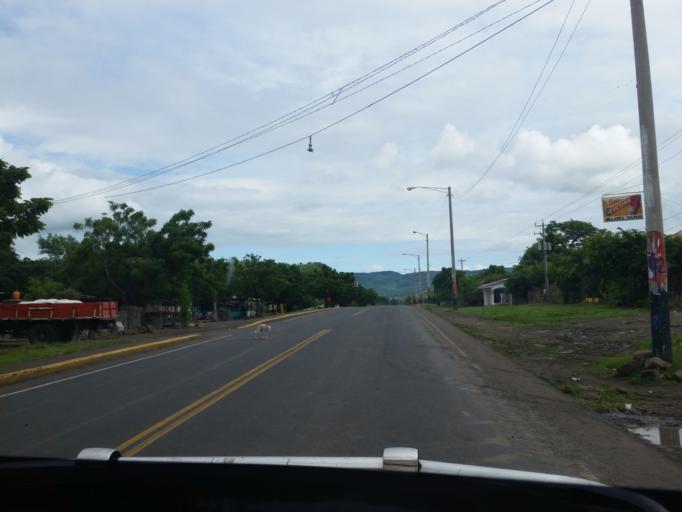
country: NI
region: Boaco
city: Teustepe
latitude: 12.4418
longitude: -86.0419
